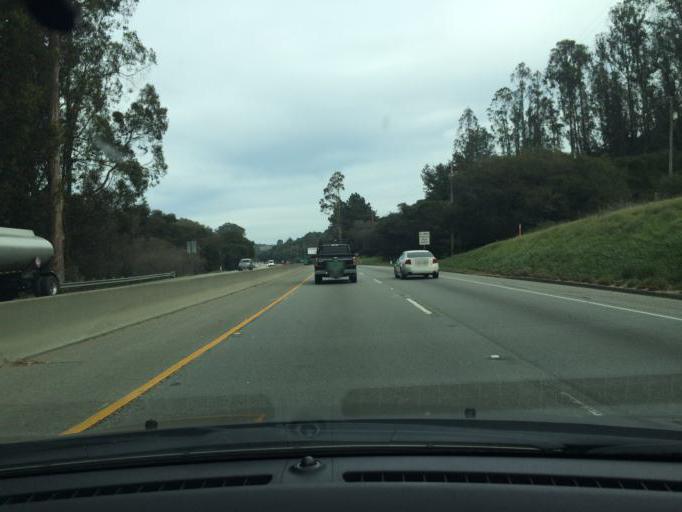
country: US
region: California
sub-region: Monterey County
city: Prunedale
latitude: 36.8048
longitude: -121.6509
